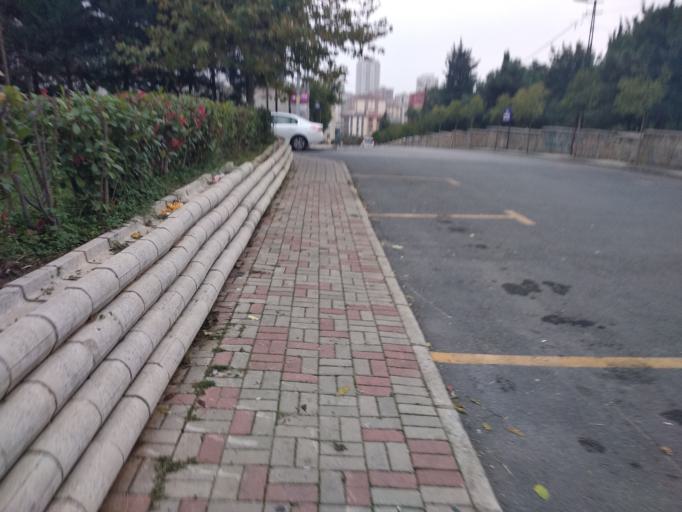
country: TR
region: Istanbul
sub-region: Atasehir
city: Atasehir
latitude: 40.9857
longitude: 29.1199
